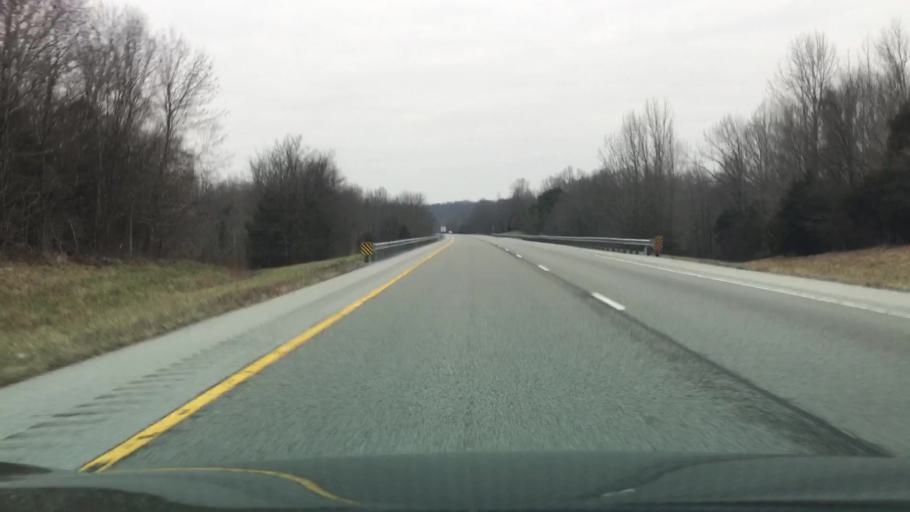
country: US
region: Illinois
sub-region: Johnson County
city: Vienna
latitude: 37.3690
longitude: -88.8044
